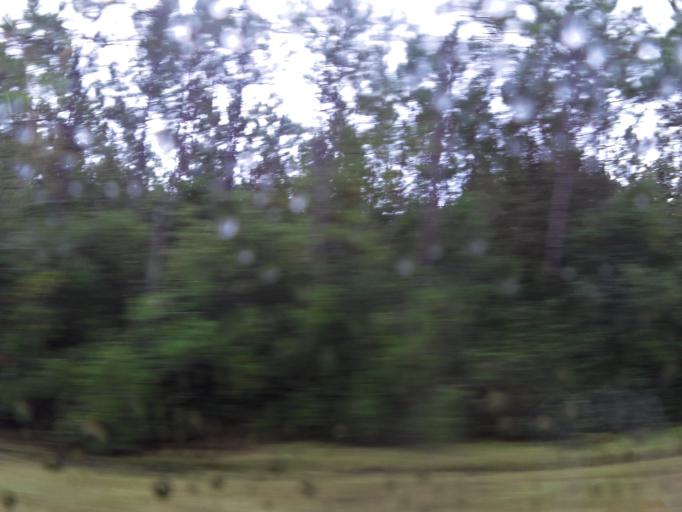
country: US
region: Florida
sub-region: Duval County
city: Baldwin
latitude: 30.4613
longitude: -82.0631
